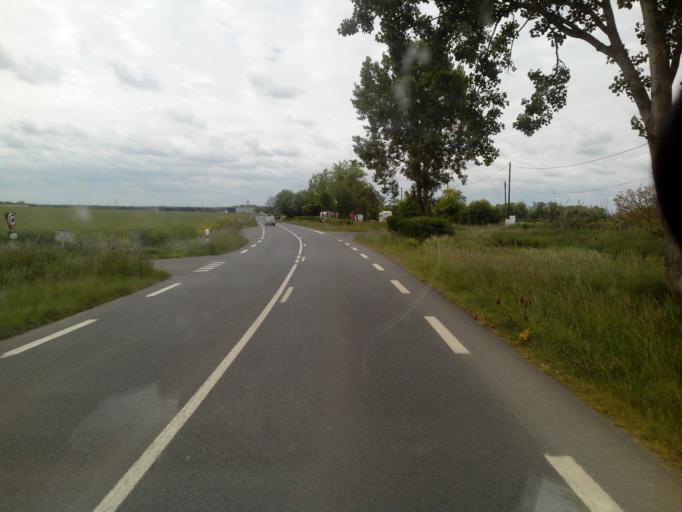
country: FR
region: Lower Normandy
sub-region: Departement du Calvados
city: Ranville
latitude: 49.2455
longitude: -0.2511
